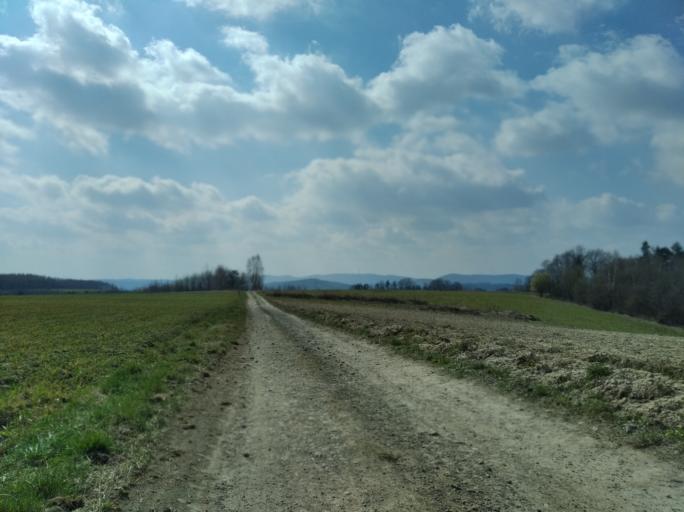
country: PL
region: Subcarpathian Voivodeship
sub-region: Powiat strzyzowski
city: Jawornik
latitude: 49.8282
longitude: 21.8585
